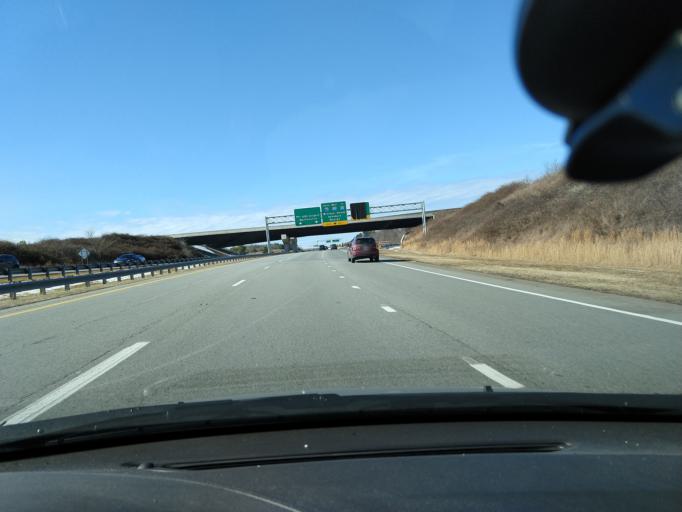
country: US
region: North Carolina
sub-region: Guilford County
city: Summerfield
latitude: 36.1159
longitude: -79.9035
